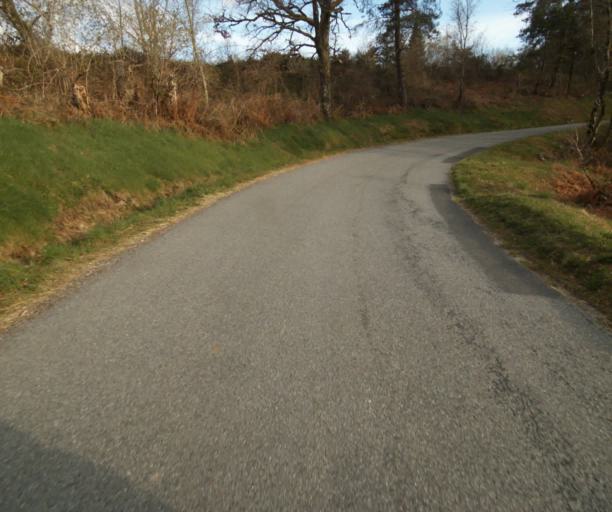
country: FR
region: Limousin
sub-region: Departement de la Correze
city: Correze
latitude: 45.4147
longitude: 1.9083
